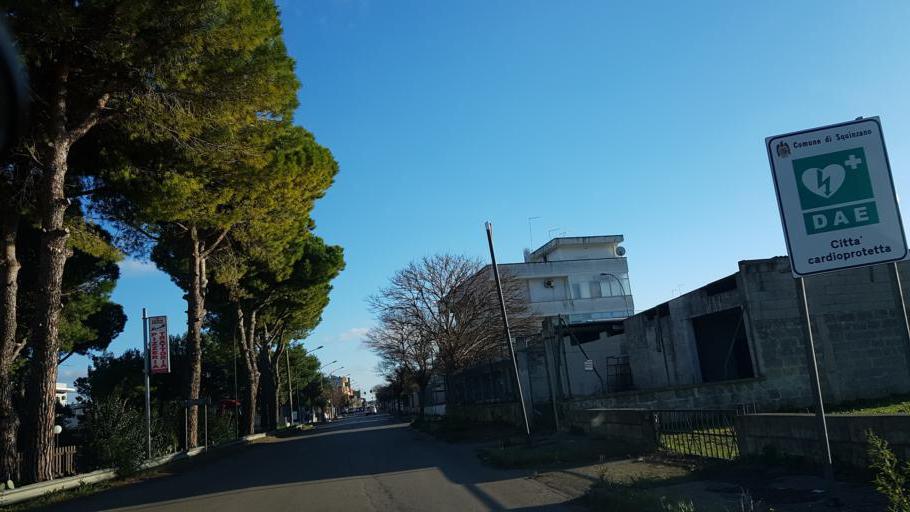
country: IT
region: Apulia
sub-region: Provincia di Lecce
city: Squinzano
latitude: 40.4435
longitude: 18.0340
